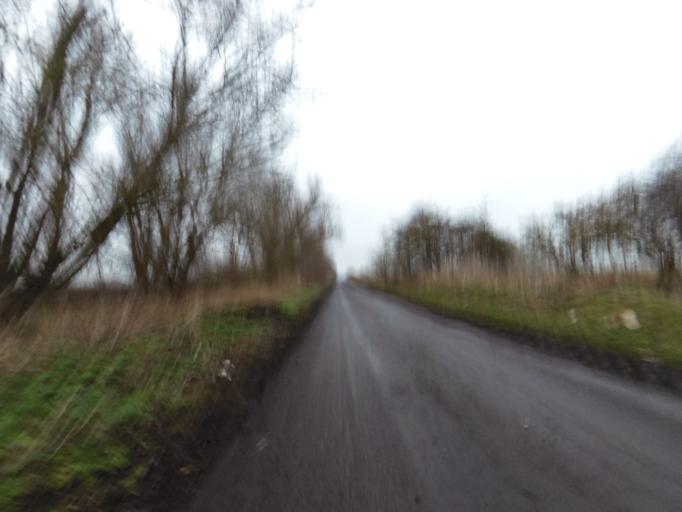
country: GB
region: England
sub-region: Cambridgeshire
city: Bottisham
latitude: 52.2789
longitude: 0.2665
